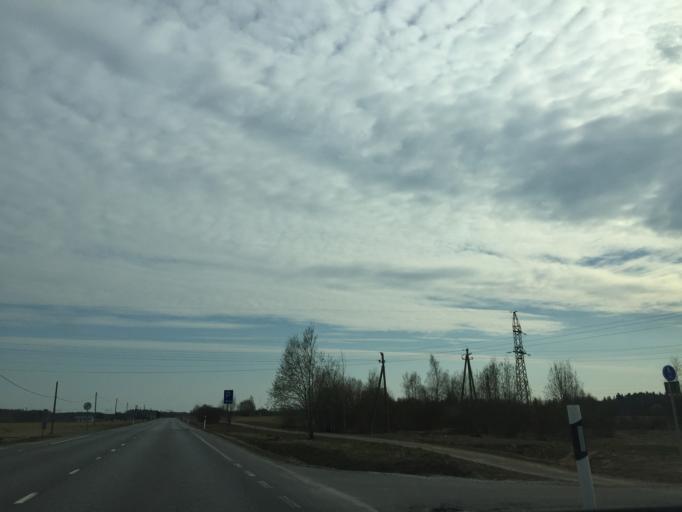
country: EE
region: Ida-Virumaa
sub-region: Johvi vald
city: Johvi
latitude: 59.2692
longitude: 27.5134
